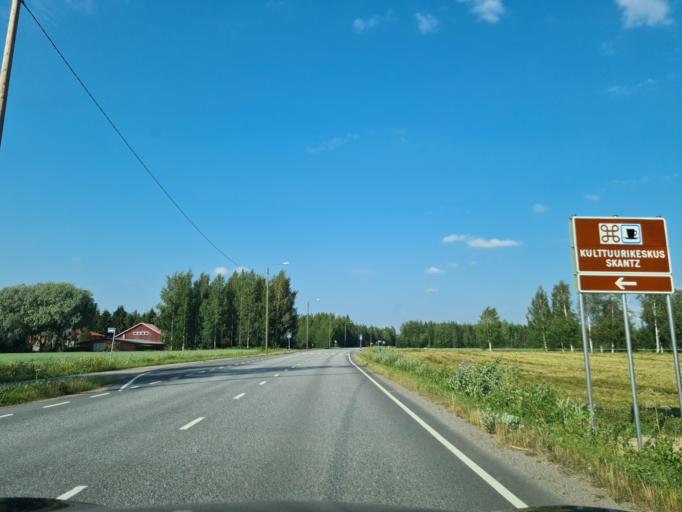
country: FI
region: Satakunta
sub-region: Pohjois-Satakunta
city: Karvia
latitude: 62.0763
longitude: 22.5122
